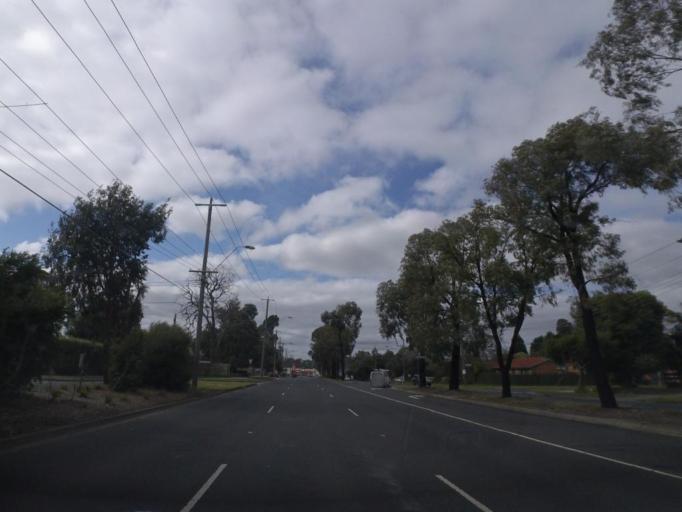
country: AU
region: Victoria
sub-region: Whitehorse
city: Vermont
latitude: -37.8329
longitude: 145.2102
